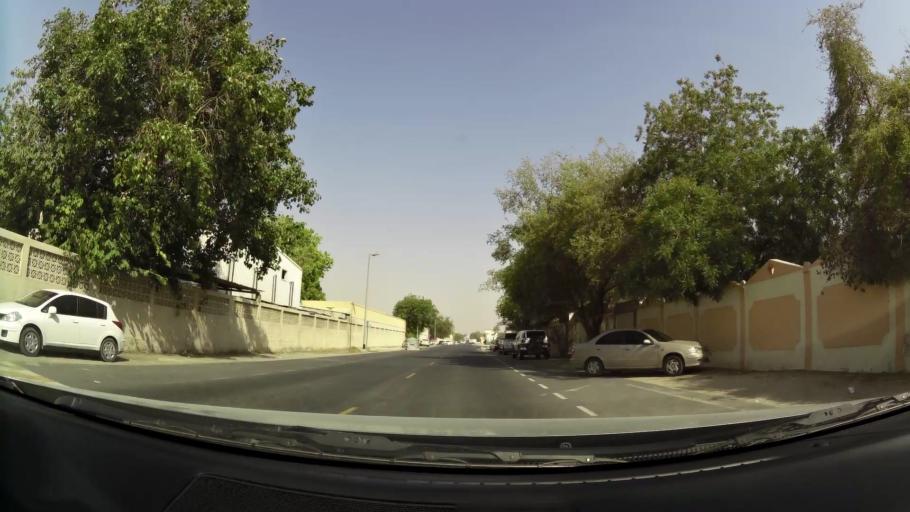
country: AE
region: Dubai
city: Dubai
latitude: 25.1768
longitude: 55.2512
